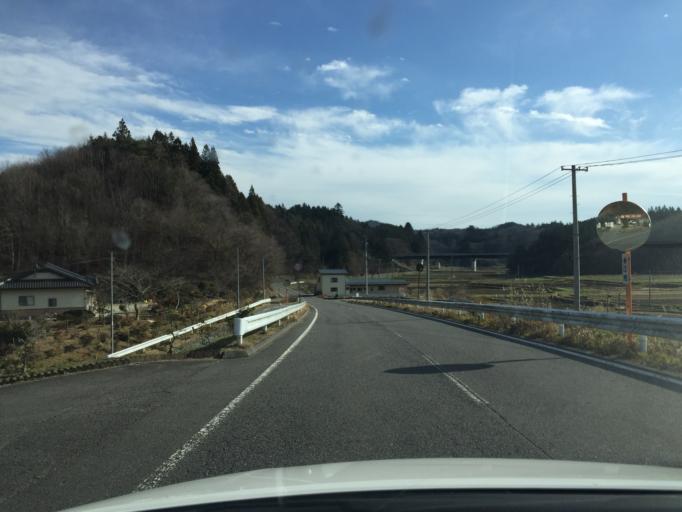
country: JP
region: Fukushima
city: Funehikimachi-funehiki
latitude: 37.2784
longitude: 140.5905
